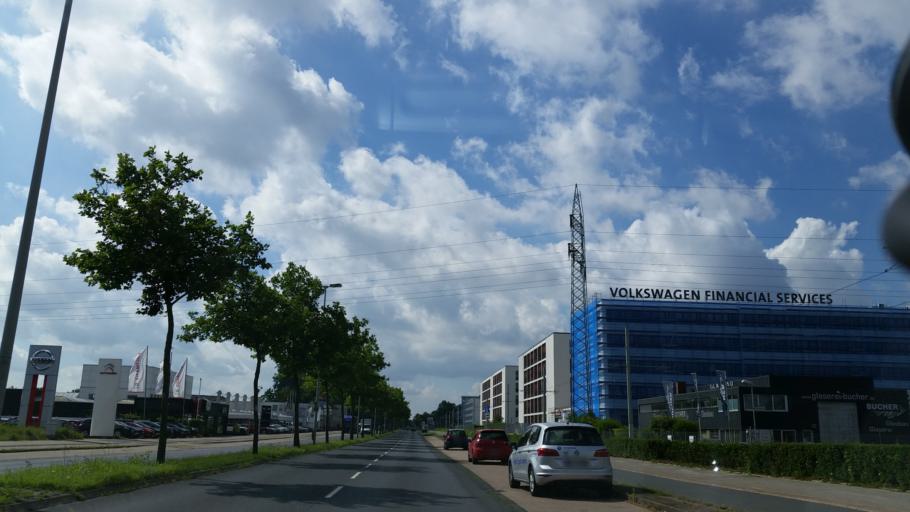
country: DE
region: Lower Saxony
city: Braunschweig
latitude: 52.3018
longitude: 10.5165
